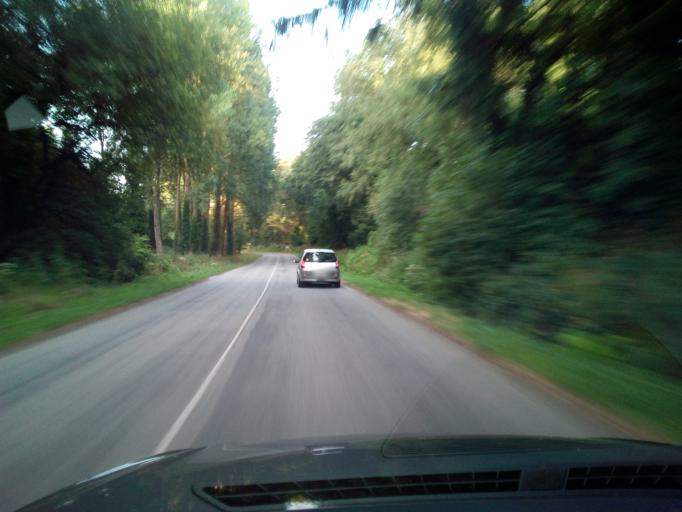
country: FR
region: Brittany
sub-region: Departement du Finistere
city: Landivisiau
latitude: 48.5018
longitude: -4.0881
